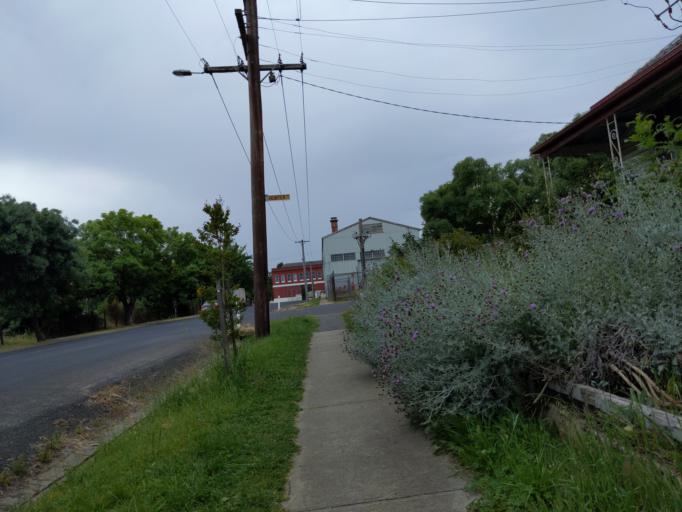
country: AU
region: Victoria
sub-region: Mount Alexander
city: Castlemaine
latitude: -37.0574
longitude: 144.2157
